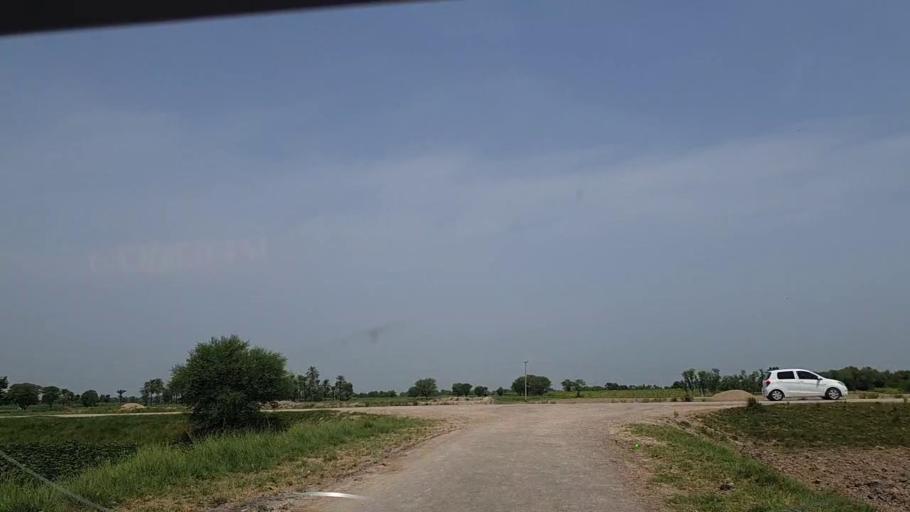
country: PK
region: Sindh
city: Tharu Shah
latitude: 26.9211
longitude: 68.0529
